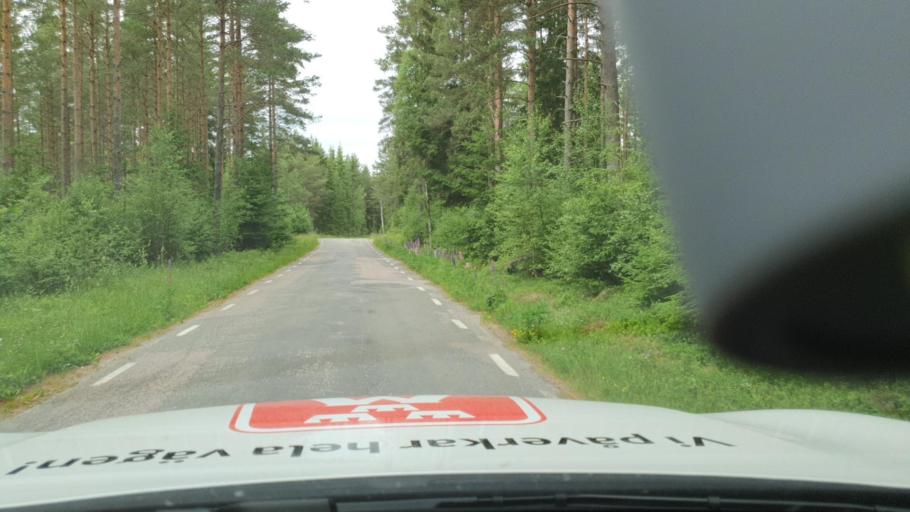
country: SE
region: Vaestra Goetaland
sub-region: Tidaholms Kommun
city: Tidaholm
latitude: 58.1746
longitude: 14.0125
